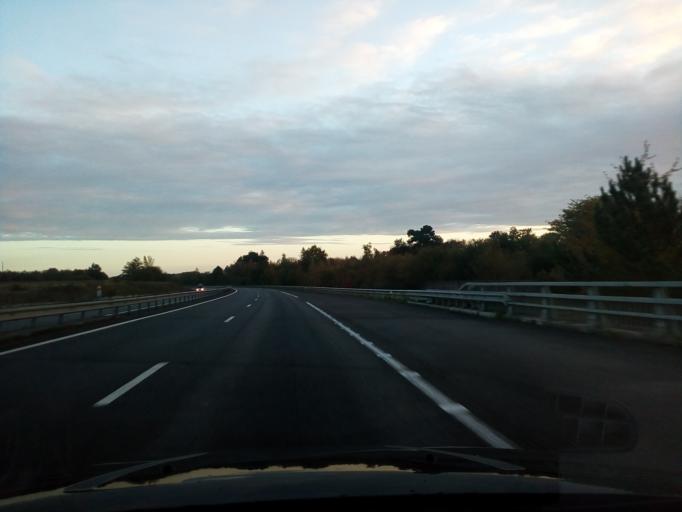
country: FR
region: Poitou-Charentes
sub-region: Departement de la Charente-Maritime
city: Montlieu-la-Garde
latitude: 45.2625
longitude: -0.2501
